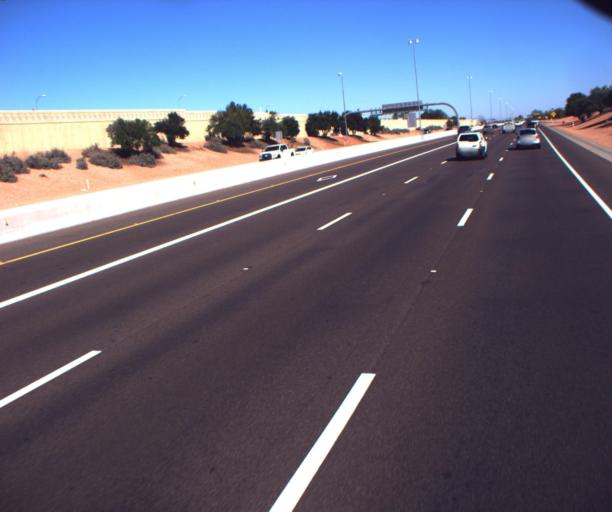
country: US
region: Arizona
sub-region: Maricopa County
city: San Carlos
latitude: 33.3219
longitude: -111.8938
